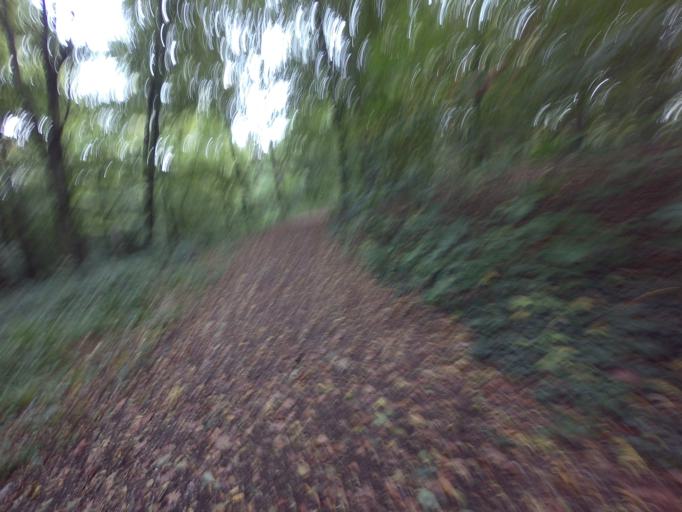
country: DE
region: North Rhine-Westphalia
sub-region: Regierungsbezirk Koln
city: Ubach-Palenberg
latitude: 50.9127
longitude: 6.0944
